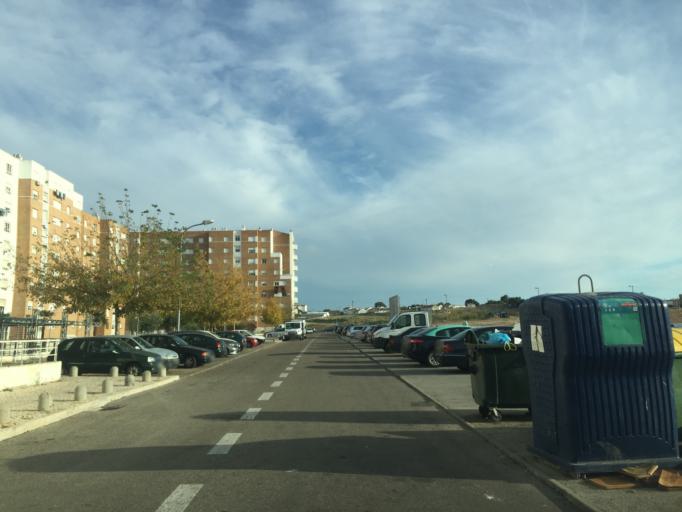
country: PT
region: Lisbon
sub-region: Odivelas
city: Olival do Basto
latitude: 38.7782
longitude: -9.1483
